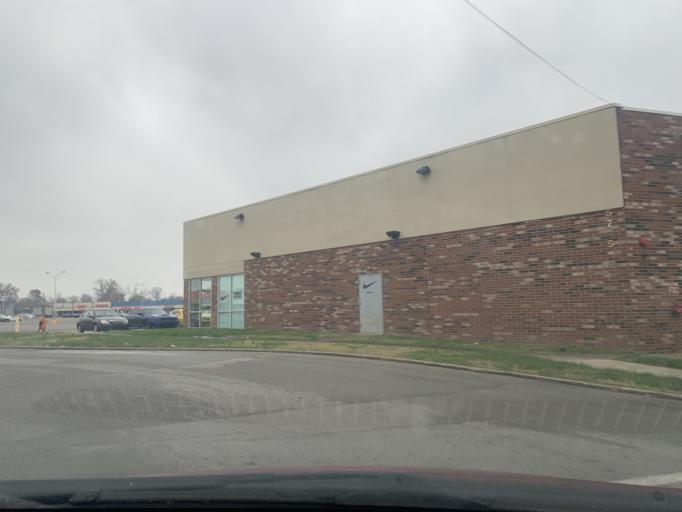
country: US
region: Kentucky
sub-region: Jefferson County
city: Okolona
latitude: 38.1665
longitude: -85.7040
